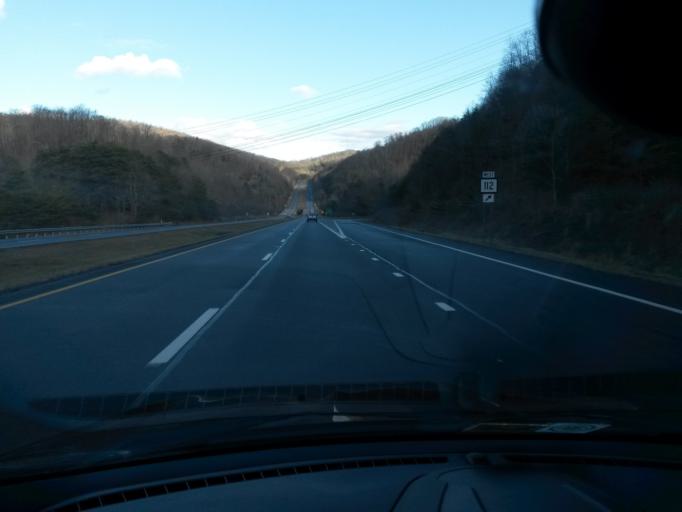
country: US
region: West Virginia
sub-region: Mercer County
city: Athens
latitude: 37.3415
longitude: -80.9617
